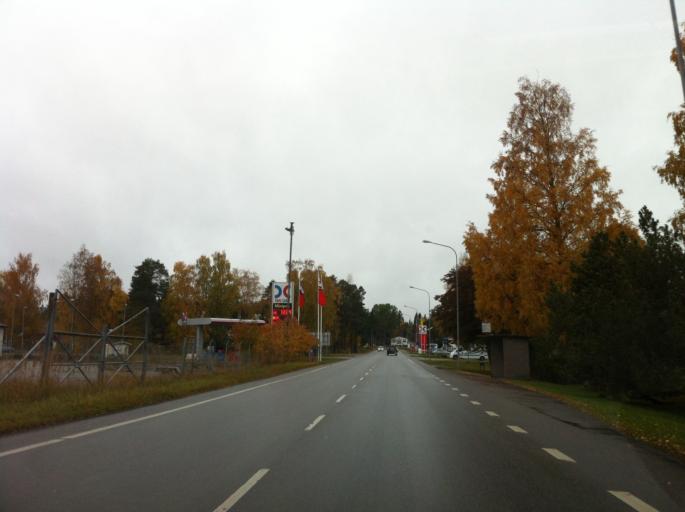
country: SE
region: Uppsala
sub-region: Osthammars Kommun
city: OEsthammar
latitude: 60.2568
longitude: 18.3507
